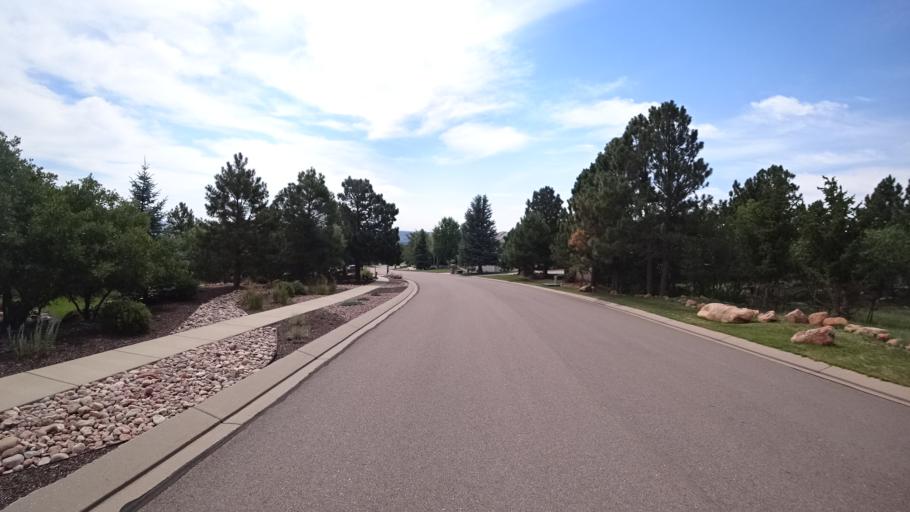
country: US
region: Colorado
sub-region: El Paso County
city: Air Force Academy
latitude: 38.9535
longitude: -104.8854
